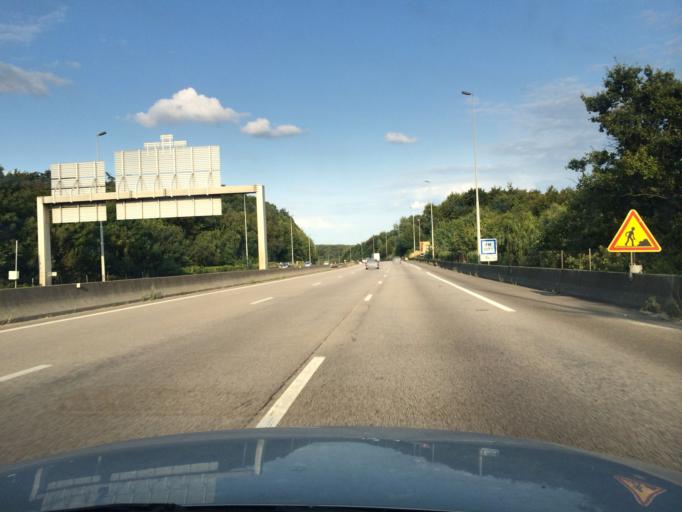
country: FR
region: Haute-Normandie
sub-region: Departement de la Seine-Maritime
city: Sahurs
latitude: 49.3392
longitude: 0.9483
